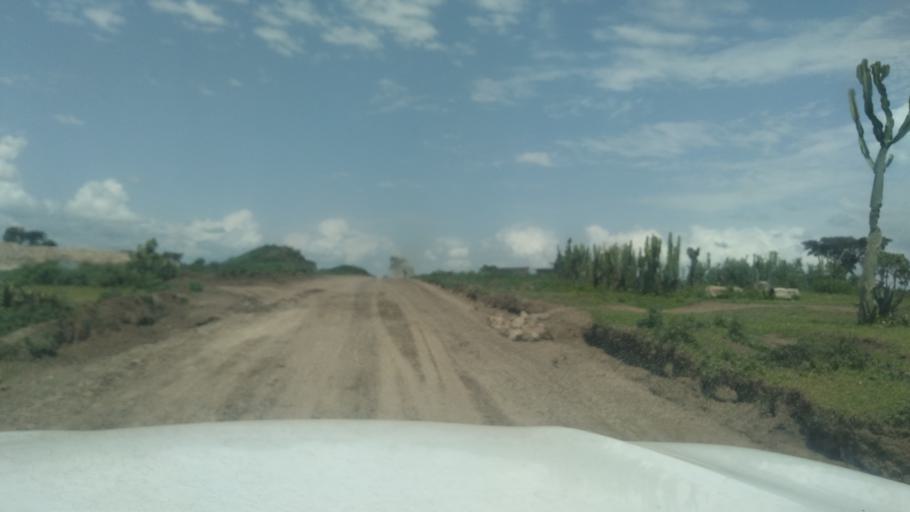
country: ET
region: Oromiya
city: Shashemene
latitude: 7.2774
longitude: 38.6032
